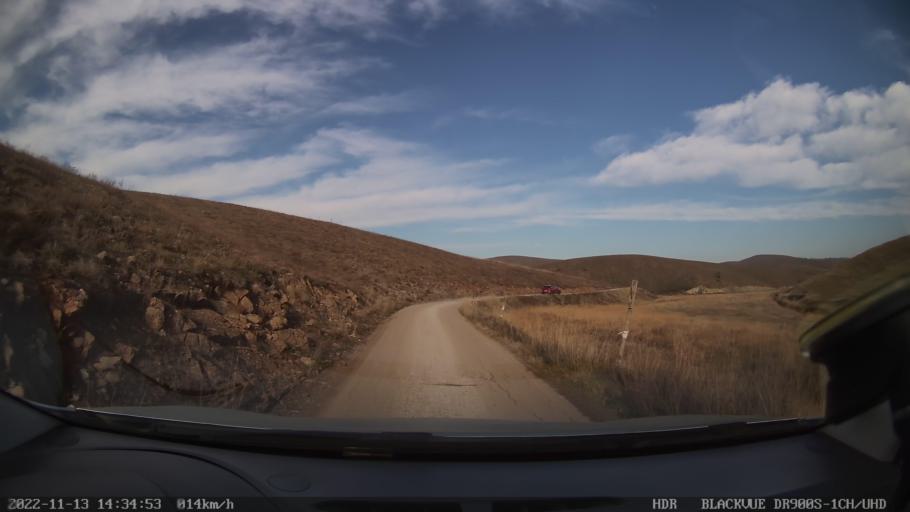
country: RS
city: Zlatibor
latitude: 43.7058
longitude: 19.7278
